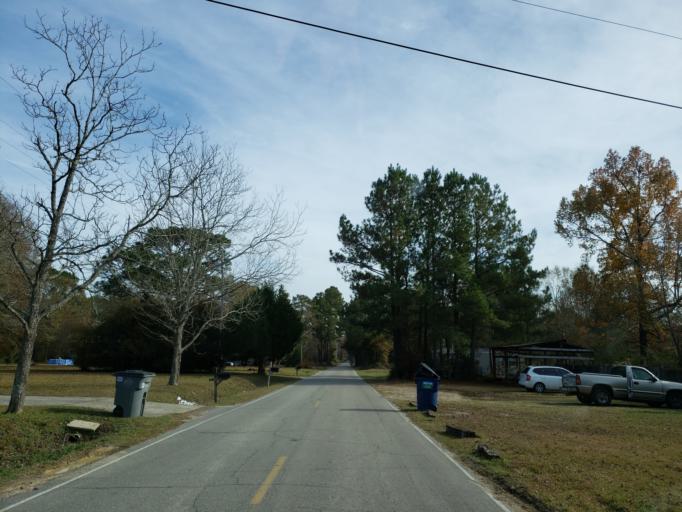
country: US
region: Mississippi
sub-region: Forrest County
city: Rawls Springs
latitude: 31.3986
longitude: -89.3915
